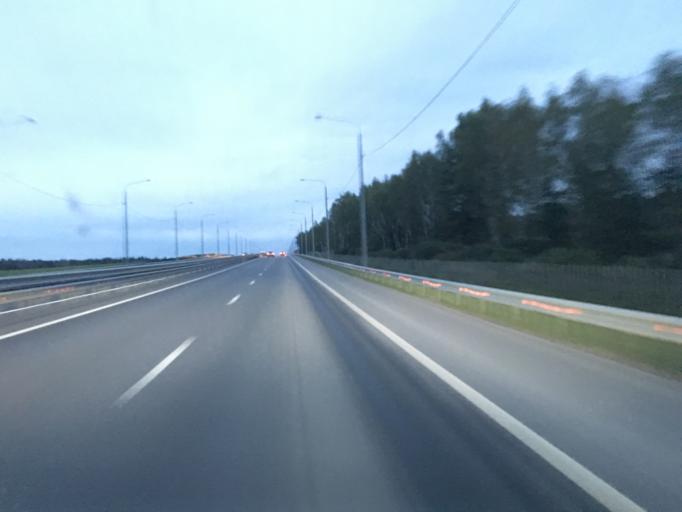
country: RU
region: Kaluga
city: Maloyaroslavets
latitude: 54.9415
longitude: 36.4316
